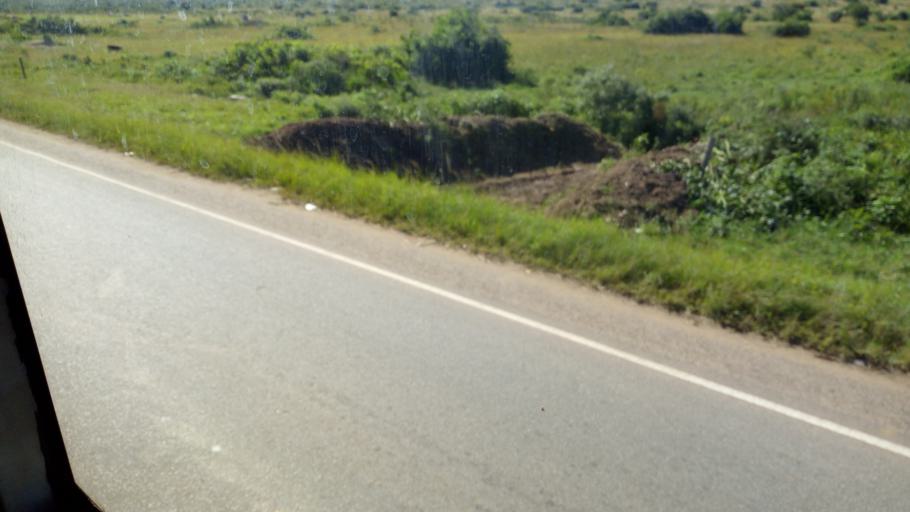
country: UG
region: Central Region
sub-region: Lyantonde District
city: Lyantonde
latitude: -0.4630
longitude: 31.0379
